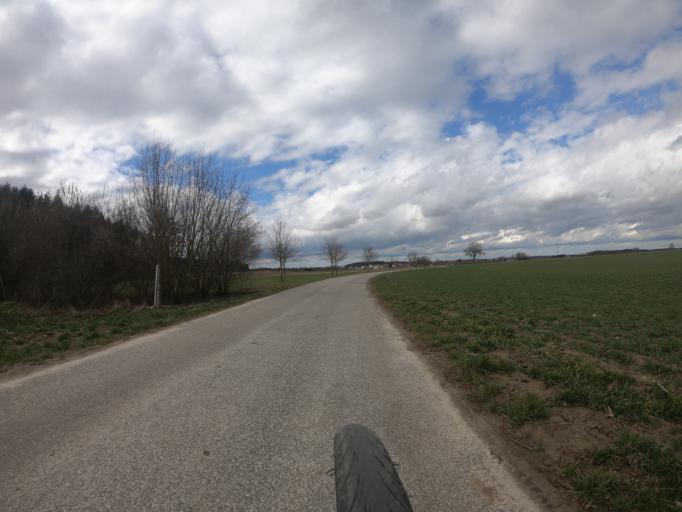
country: DE
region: Bavaria
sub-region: Upper Bavaria
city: Landsberied
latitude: 48.1721
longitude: 11.1971
